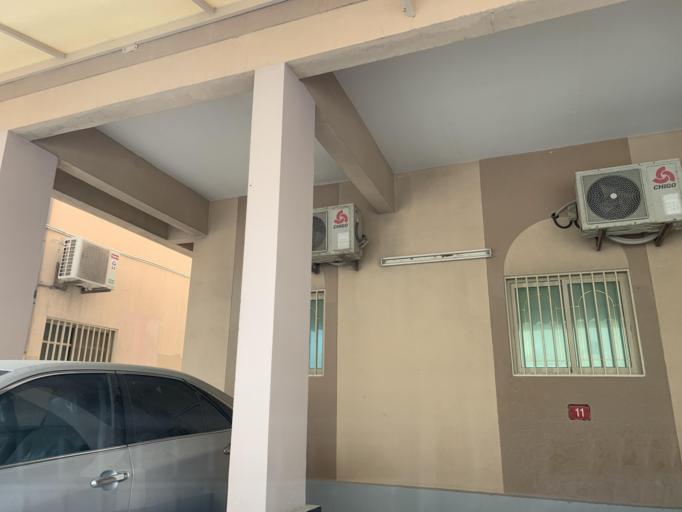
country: BH
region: Northern
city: Sitrah
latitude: 26.1376
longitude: 50.6027
